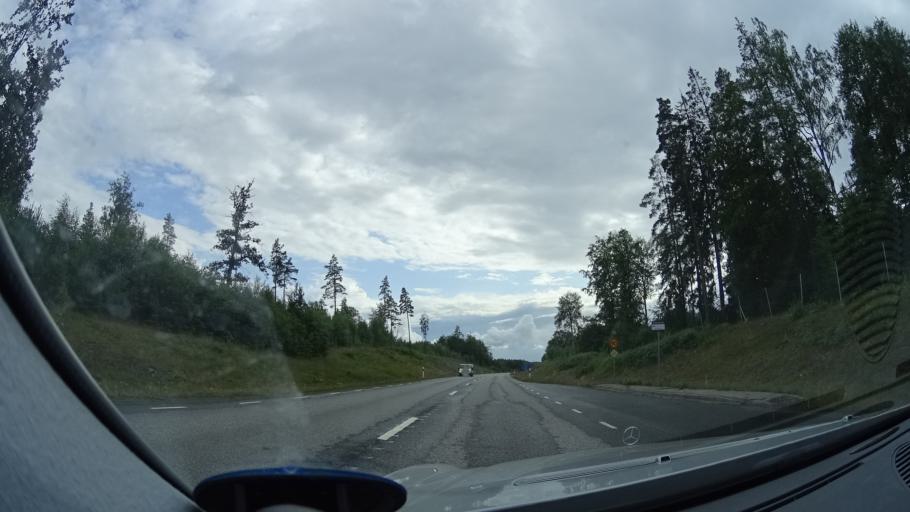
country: SE
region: Blekinge
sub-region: Karlshamns Kommun
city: Svangsta
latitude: 56.2752
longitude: 14.8614
